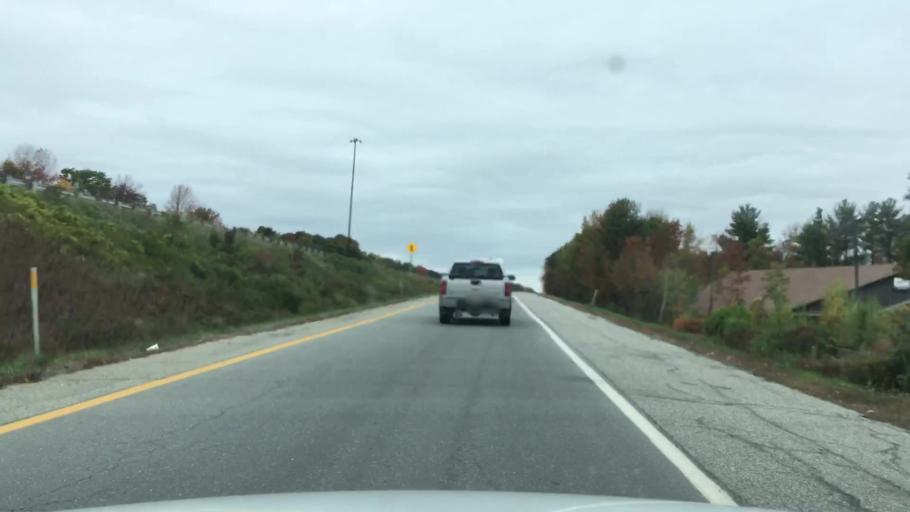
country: US
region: Maine
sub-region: Kennebec County
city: Oakland
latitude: 44.5459
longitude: -69.6789
